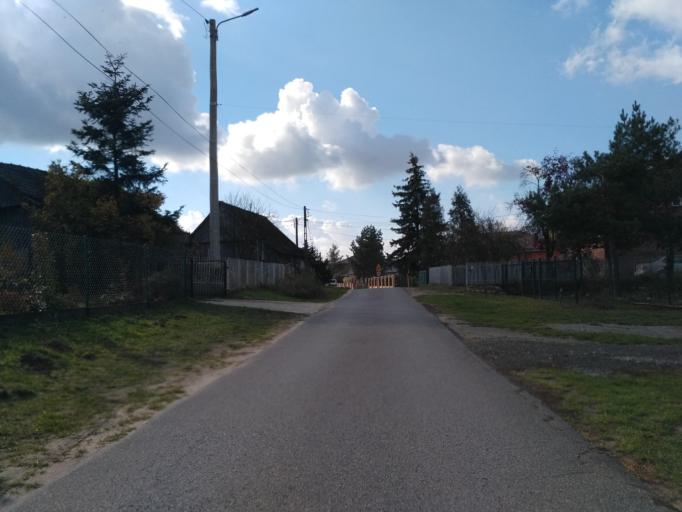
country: PL
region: Subcarpathian Voivodeship
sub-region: Powiat rzeszowski
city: Swilcza
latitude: 50.1184
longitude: 21.8846
